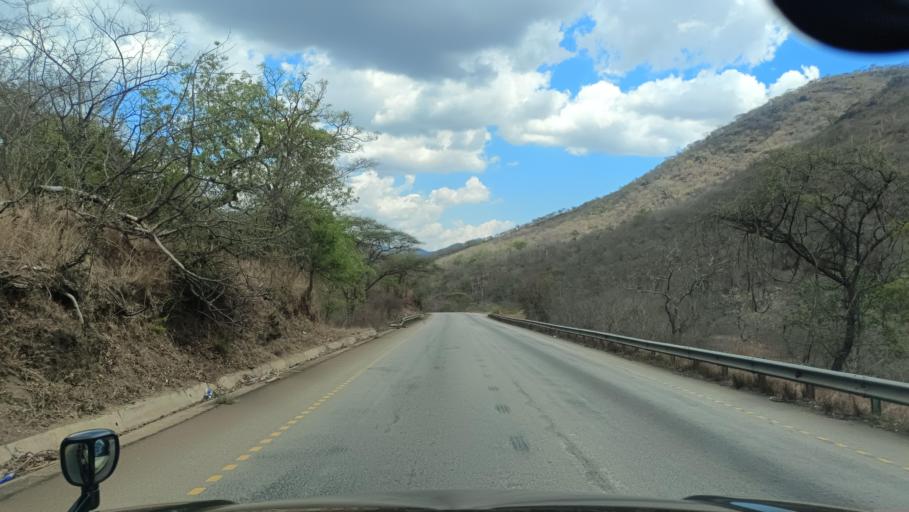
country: TZ
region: Morogoro
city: Kidatu
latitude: -7.5754
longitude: 36.7458
